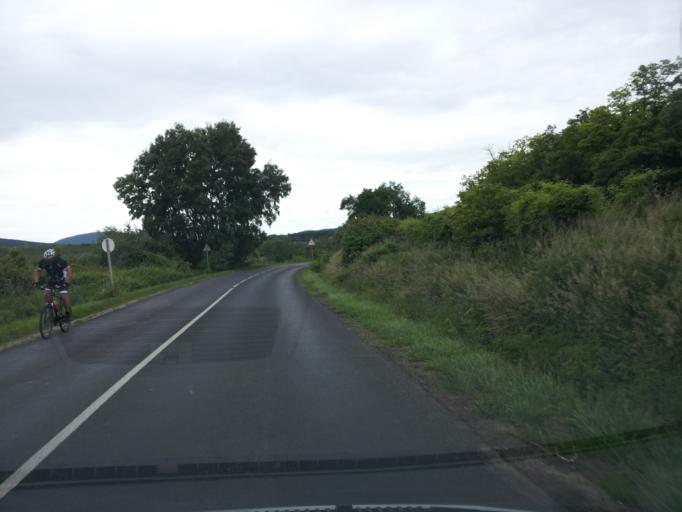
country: HU
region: Pest
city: Csobanka
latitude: 47.6567
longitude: 18.9769
